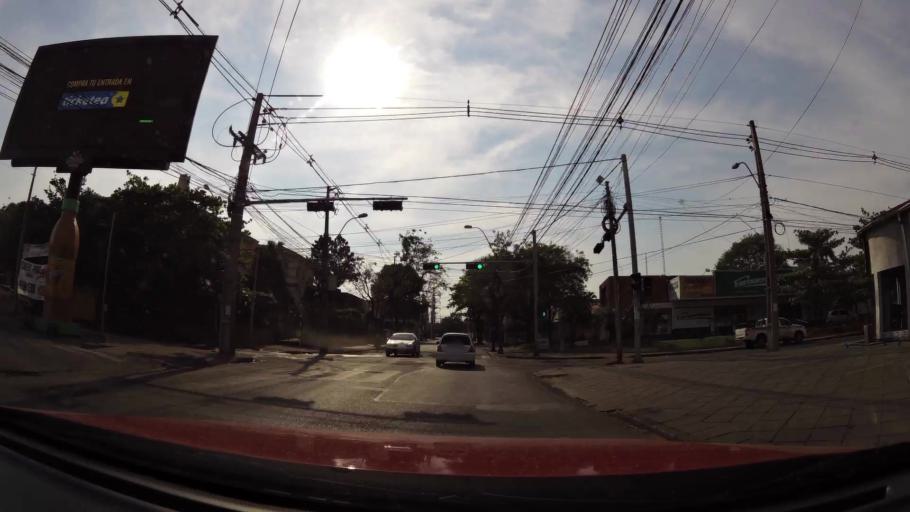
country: PY
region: Asuncion
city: Asuncion
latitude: -25.2882
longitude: -57.6058
